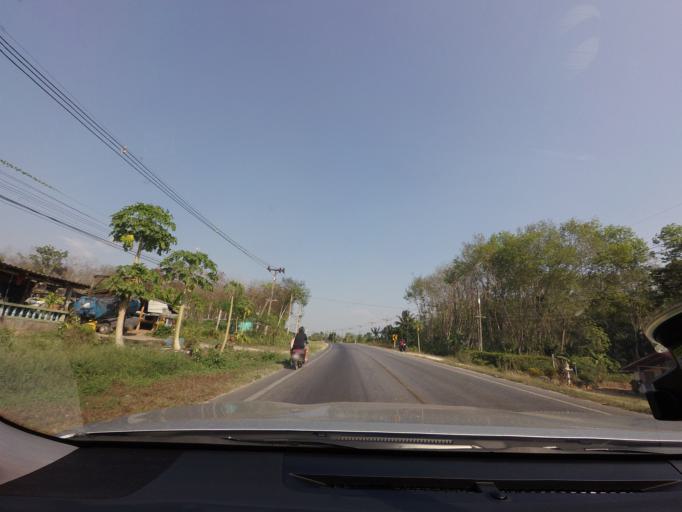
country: TH
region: Surat Thani
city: Phrasaeng
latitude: 8.5603
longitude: 99.1533
